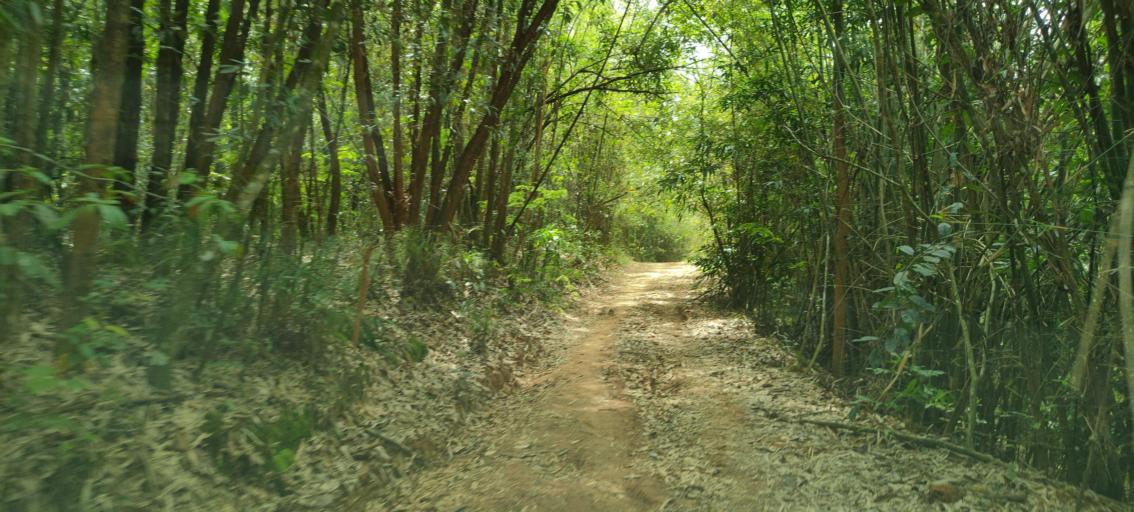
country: LA
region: Loungnamtha
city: Muang Nale
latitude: 20.4157
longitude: 101.4721
